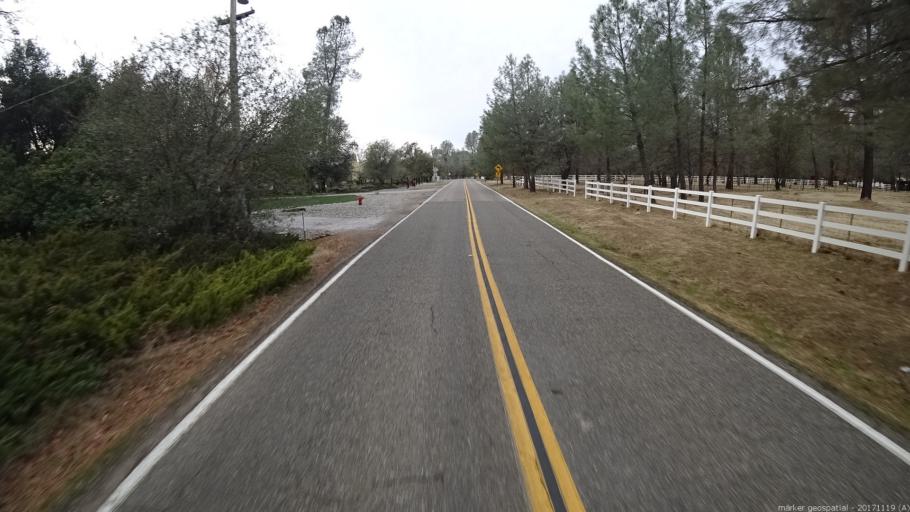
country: US
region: California
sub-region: Shasta County
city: Redding
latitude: 40.4849
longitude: -122.4531
